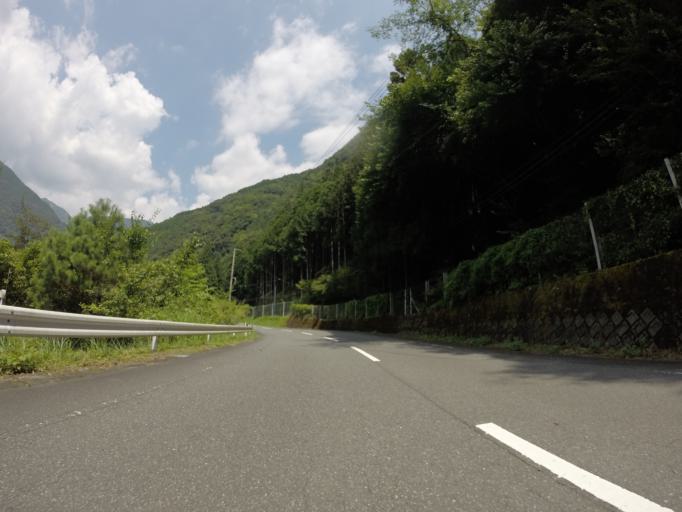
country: JP
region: Shizuoka
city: Shizuoka-shi
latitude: 35.2561
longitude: 138.3331
